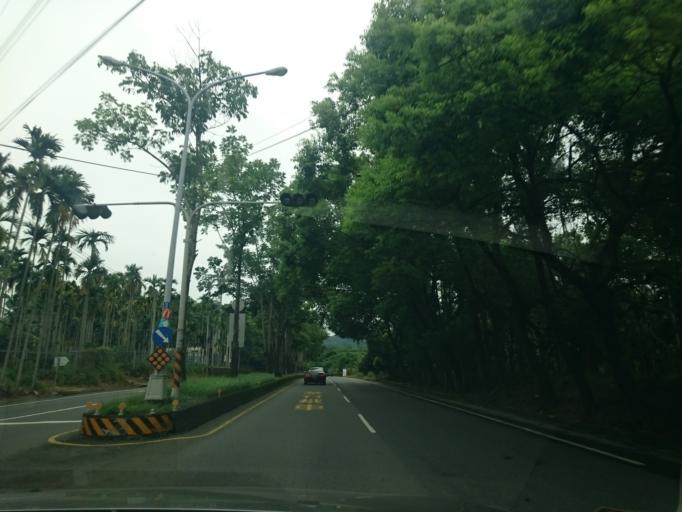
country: TW
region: Taiwan
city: Lugu
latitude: 23.8318
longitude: 120.7471
